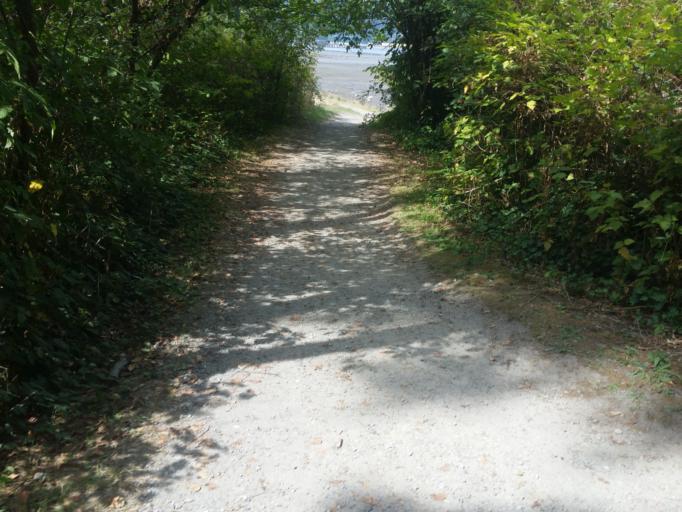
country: CA
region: British Columbia
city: Port Moody
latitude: 49.2827
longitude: -122.8352
